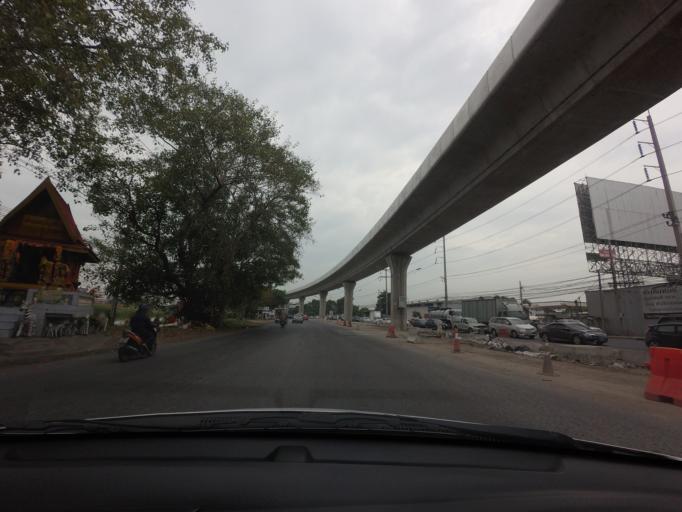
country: TH
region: Samut Prakan
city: Samut Prakan
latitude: 13.5748
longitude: 100.6048
